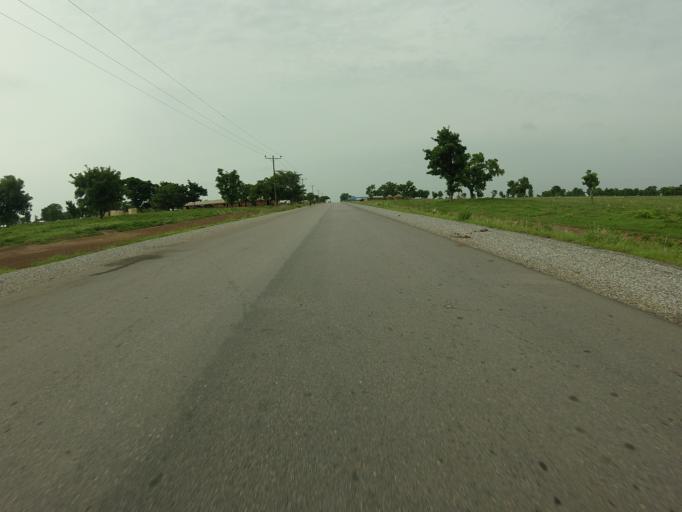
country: GH
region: Northern
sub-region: Yendi
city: Yendi
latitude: 9.8147
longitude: -0.1163
